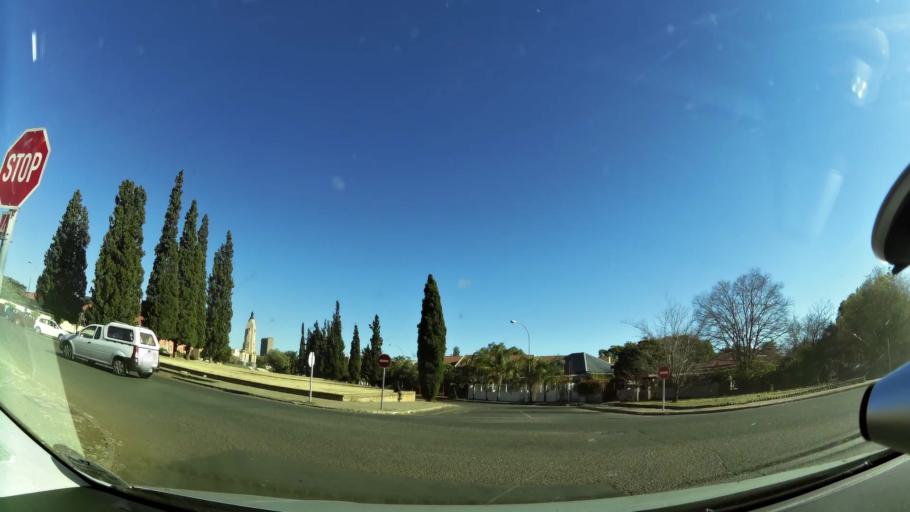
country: ZA
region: Northern Cape
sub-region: Frances Baard District Municipality
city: Kimberley
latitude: -28.7459
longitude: 24.7750
